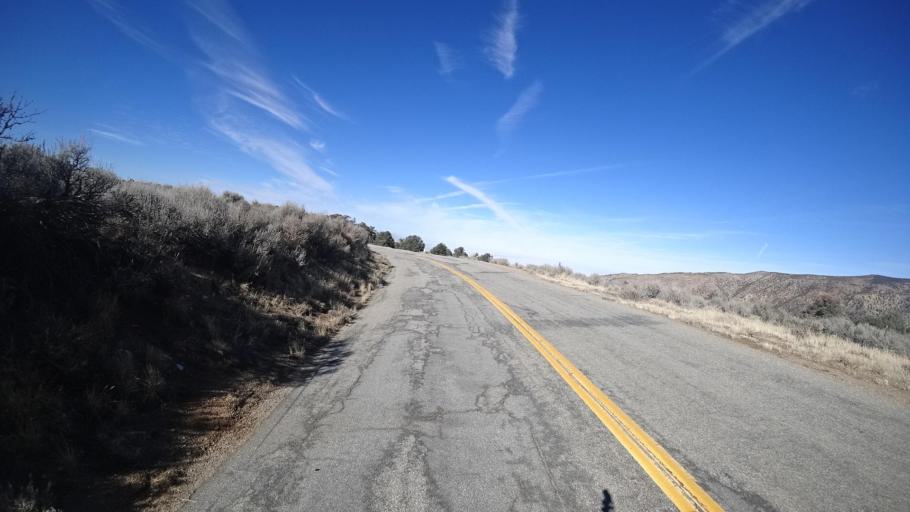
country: US
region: California
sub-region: Kern County
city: Pine Mountain Club
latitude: 34.8744
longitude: -119.2853
